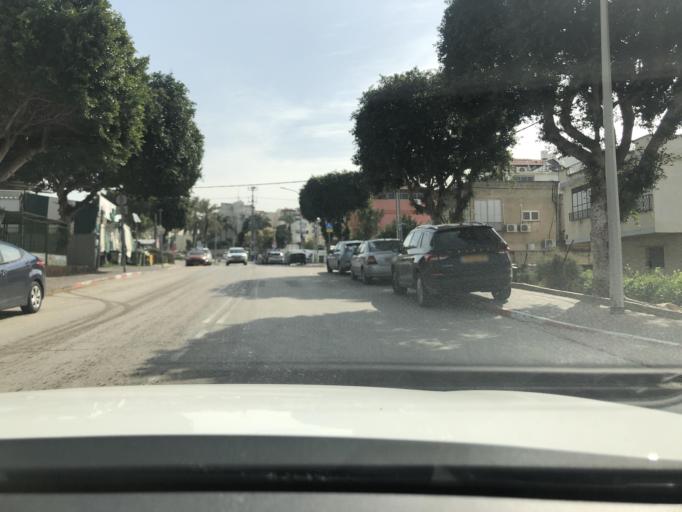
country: IL
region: Central District
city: Rosh Ha'Ayin
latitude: 32.0882
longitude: 34.9519
